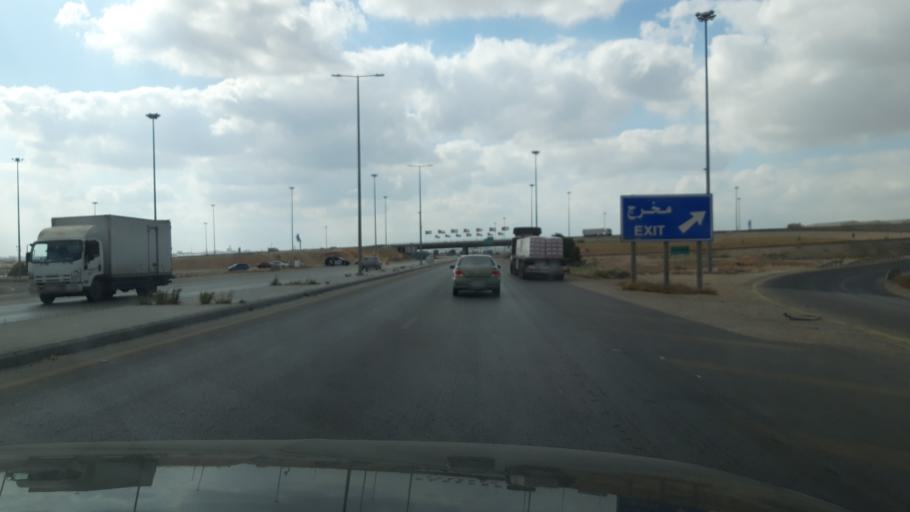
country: JO
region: Amman
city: Sahab
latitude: 31.8446
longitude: 36.0439
